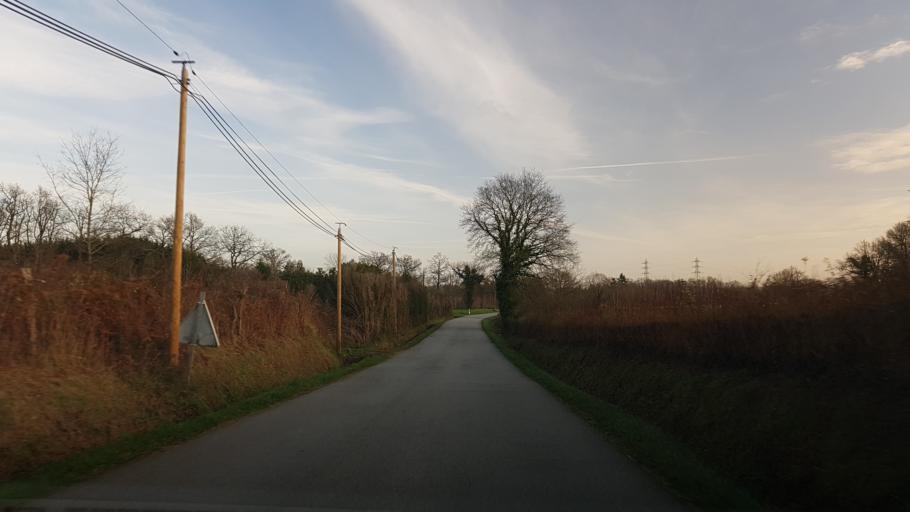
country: FR
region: Poitou-Charentes
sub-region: Departement de la Charente
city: Brigueuil
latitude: 45.9061
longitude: 0.8518
